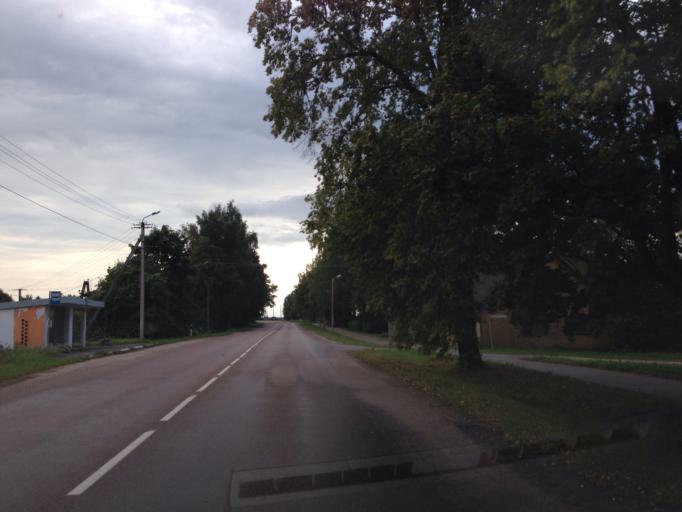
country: EE
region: Tartu
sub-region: Puhja vald
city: Puhja
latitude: 58.1795
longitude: 26.1989
